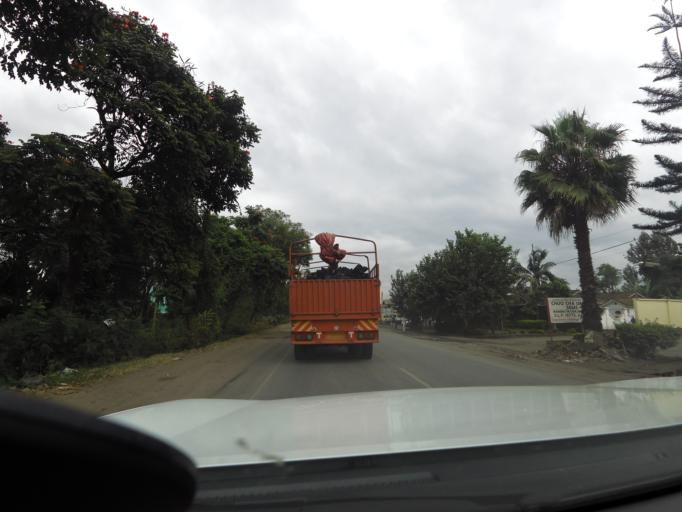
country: TZ
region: Arusha
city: Arusha
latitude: -3.3624
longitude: 36.6809
